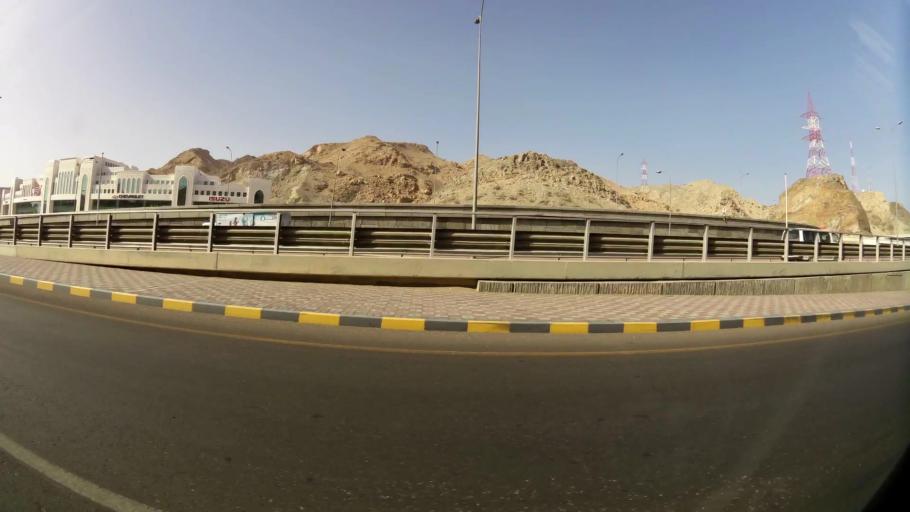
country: OM
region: Muhafazat Masqat
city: Muscat
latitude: 23.5923
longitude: 58.5244
